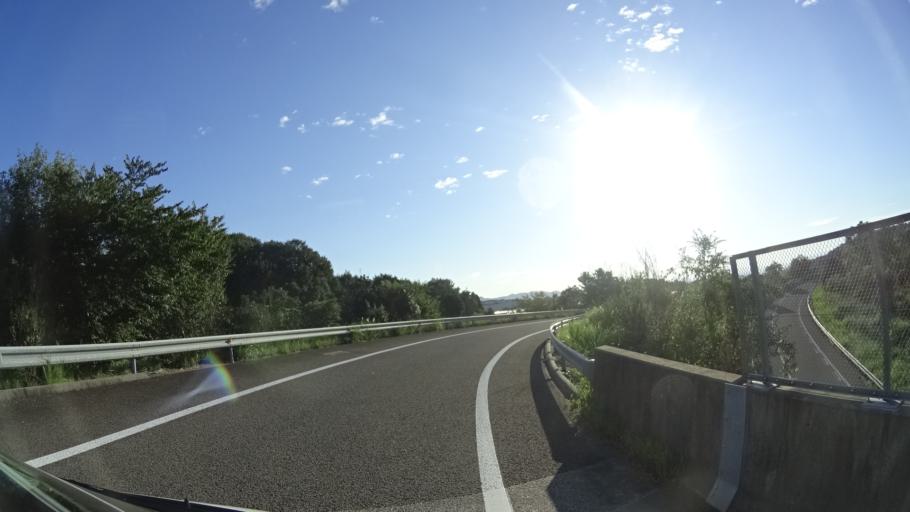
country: JP
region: Gifu
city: Minokamo
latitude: 35.4699
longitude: 137.0224
